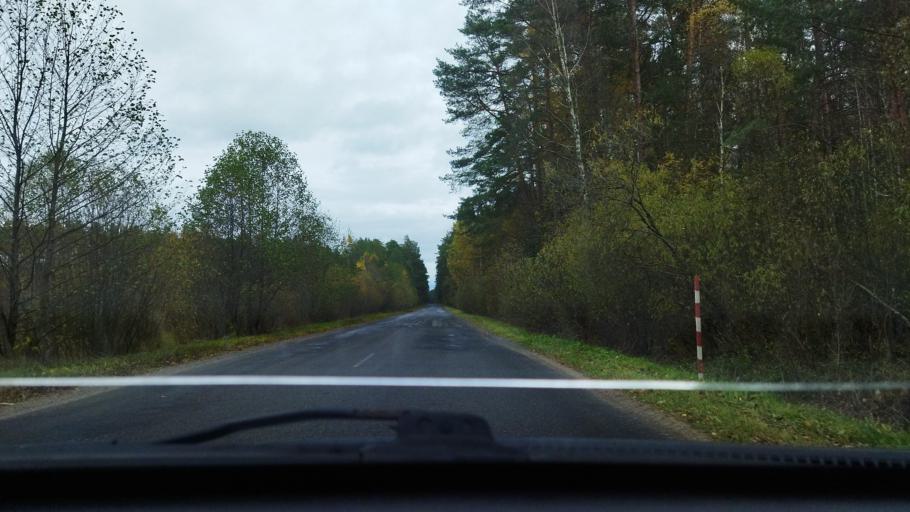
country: BY
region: Minsk
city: Svir
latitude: 54.8124
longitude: 26.2023
